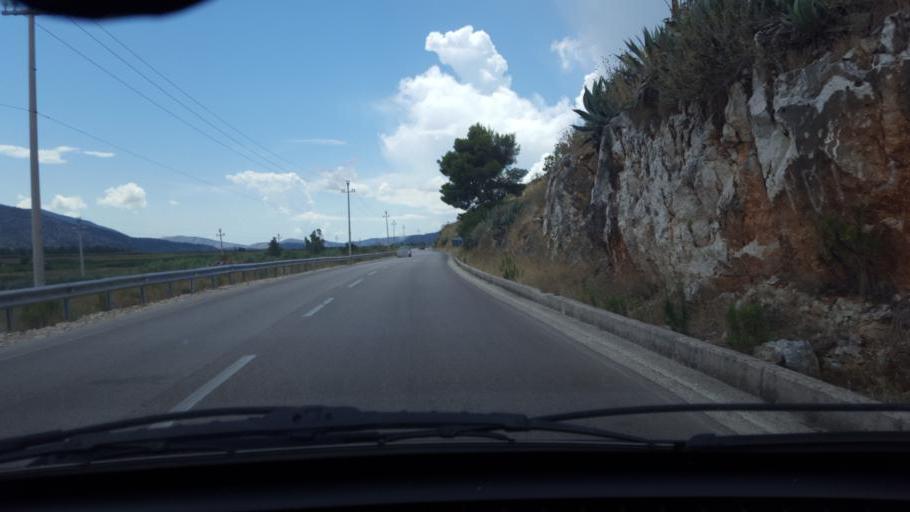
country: AL
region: Vlore
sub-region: Rrethi i Sarandes
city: Sarande
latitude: 39.8324
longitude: 20.0226
